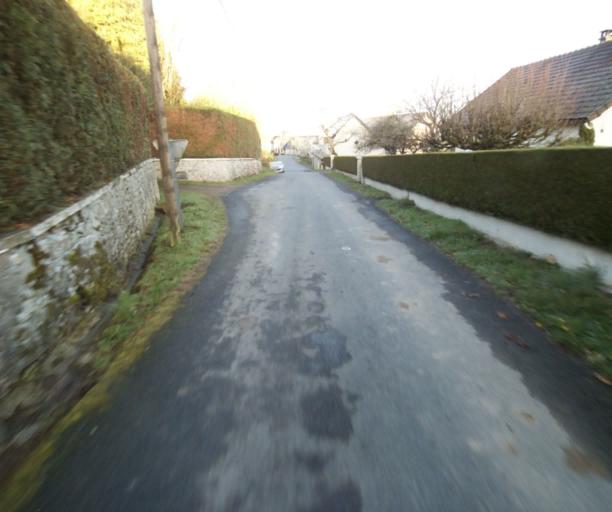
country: FR
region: Limousin
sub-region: Departement de la Correze
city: Correze
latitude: 45.3213
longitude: 1.8363
